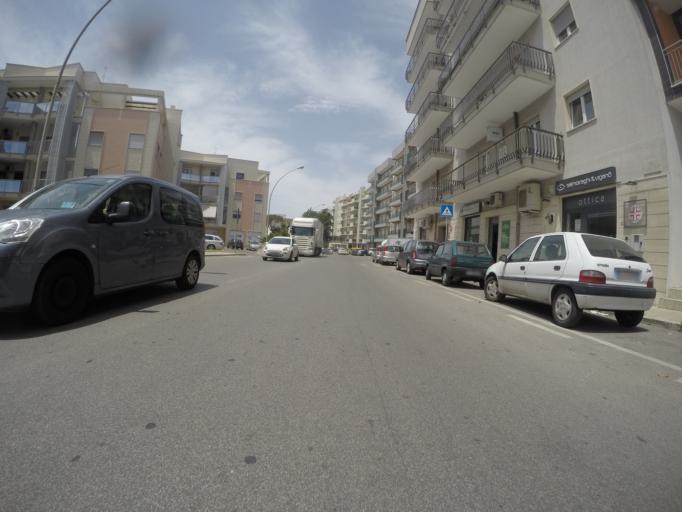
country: IT
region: Apulia
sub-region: Provincia di Taranto
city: Martina Franca
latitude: 40.6973
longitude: 17.3392
